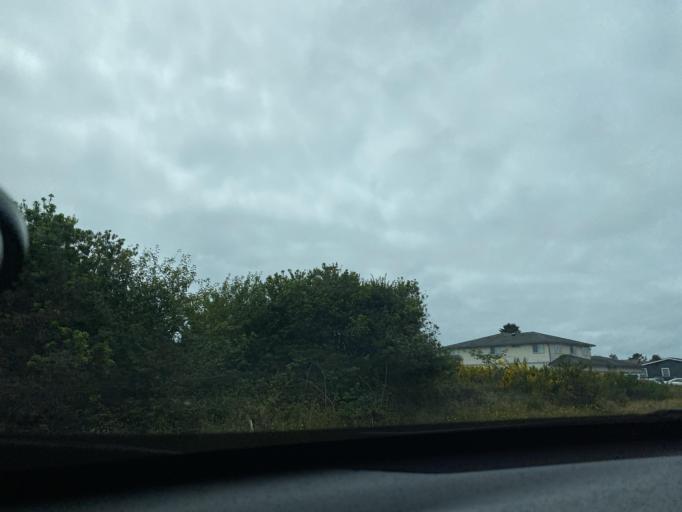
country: US
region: Washington
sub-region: Grays Harbor County
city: Ocean Shores
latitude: 46.9500
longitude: -124.1410
